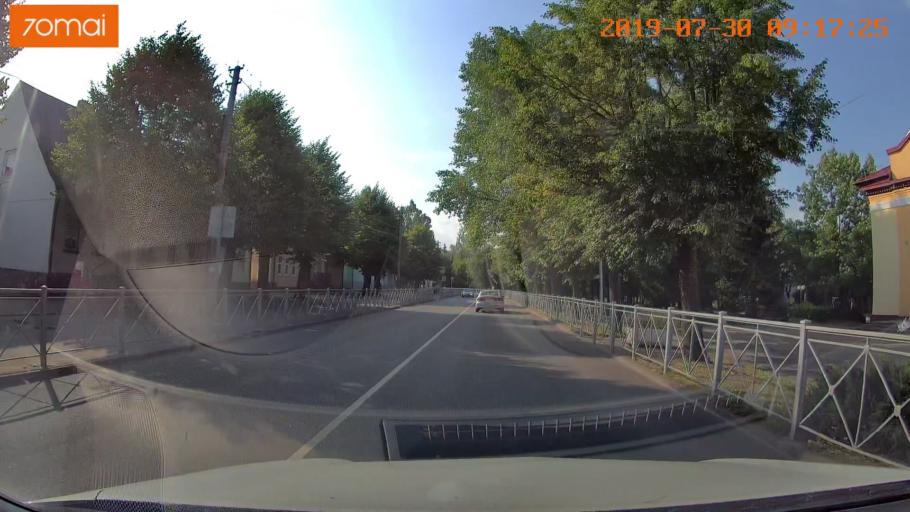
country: RU
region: Kaliningrad
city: Nesterov
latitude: 54.6339
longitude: 22.5683
